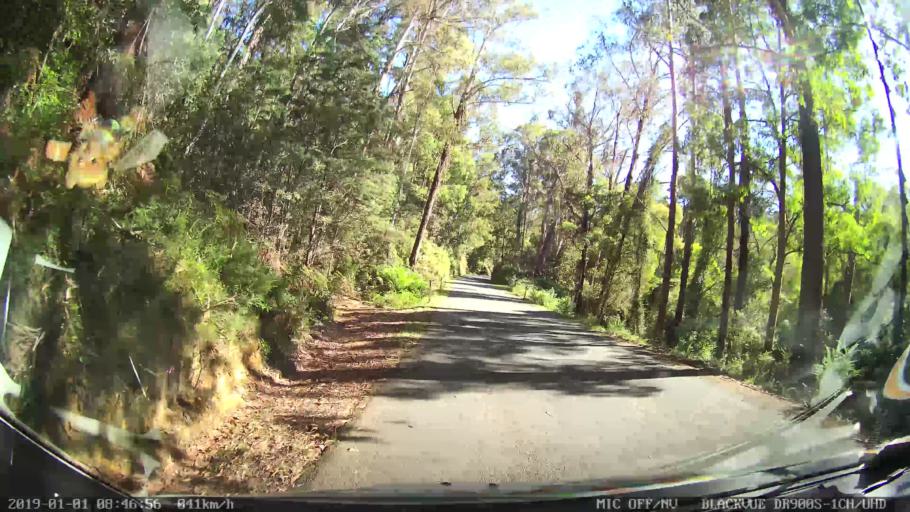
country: AU
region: New South Wales
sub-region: Snowy River
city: Jindabyne
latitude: -36.2973
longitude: 148.1952
